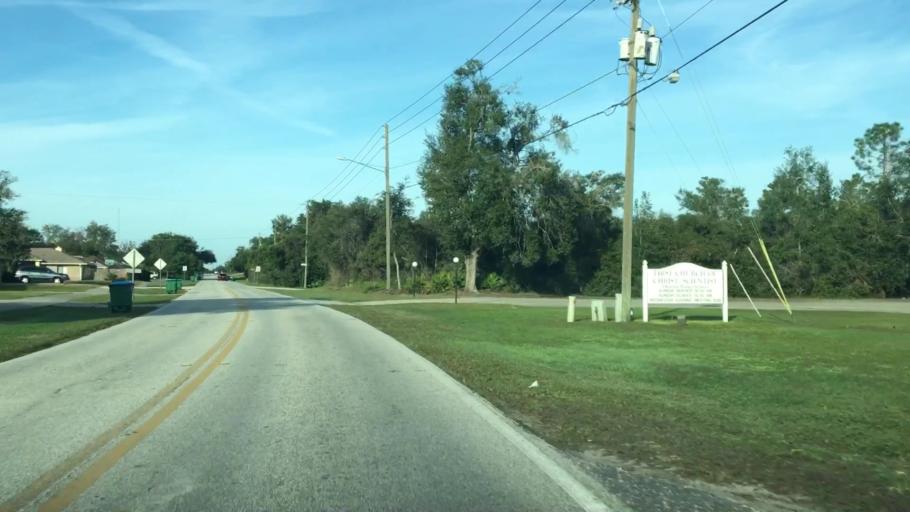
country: US
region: Florida
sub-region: Volusia County
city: Deltona
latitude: 28.9254
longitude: -81.2476
